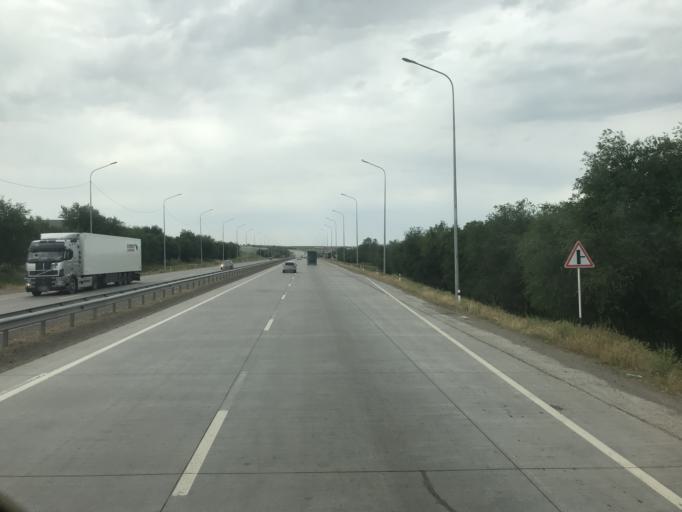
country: KZ
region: Ongtustik Qazaqstan
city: Shymkent
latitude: 42.2171
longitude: 69.5268
